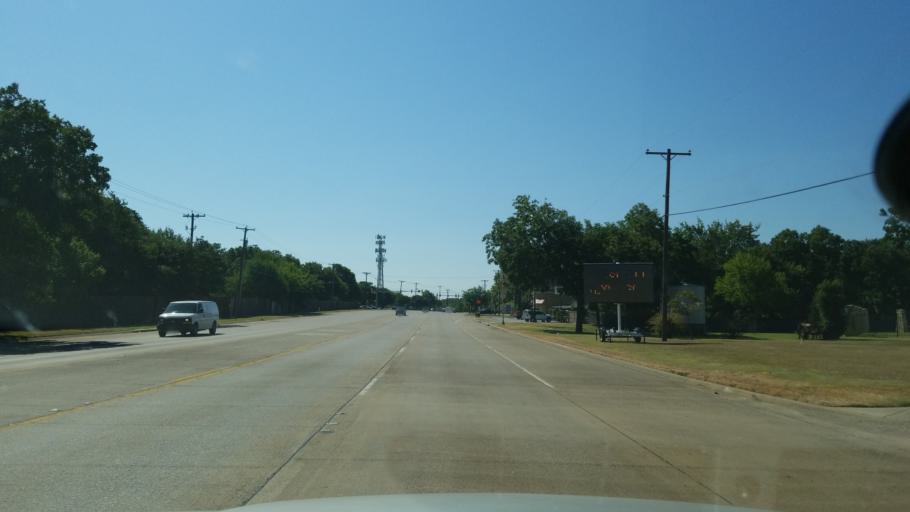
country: US
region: Texas
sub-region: Tarrant County
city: Mansfield
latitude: 32.5744
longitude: -97.1449
